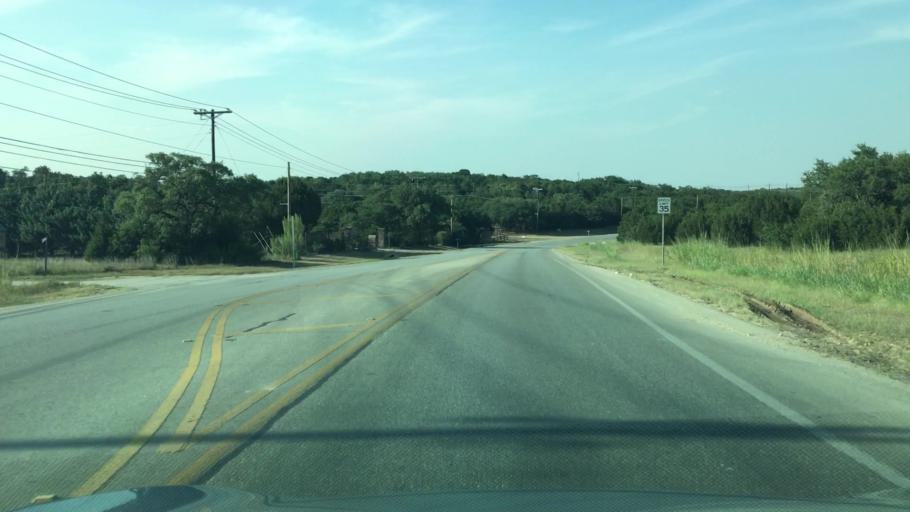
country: US
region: Texas
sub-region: Hays County
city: Dripping Springs
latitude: 30.1887
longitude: -98.0005
